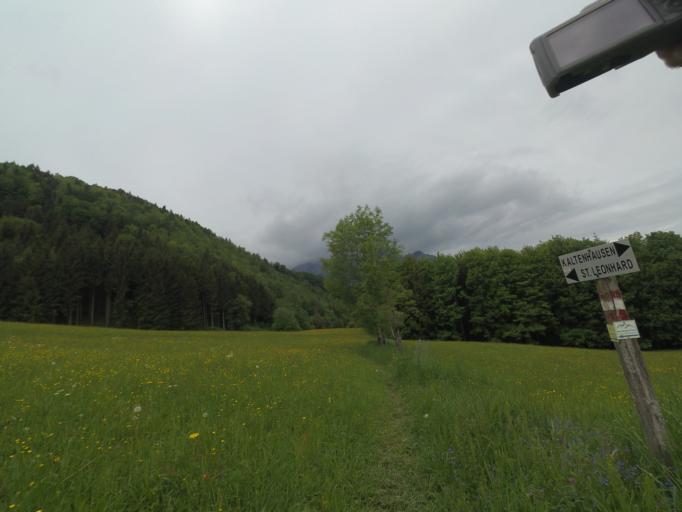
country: DE
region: Bavaria
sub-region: Upper Bavaria
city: Marktschellenberg
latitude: 47.7074
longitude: 13.0553
